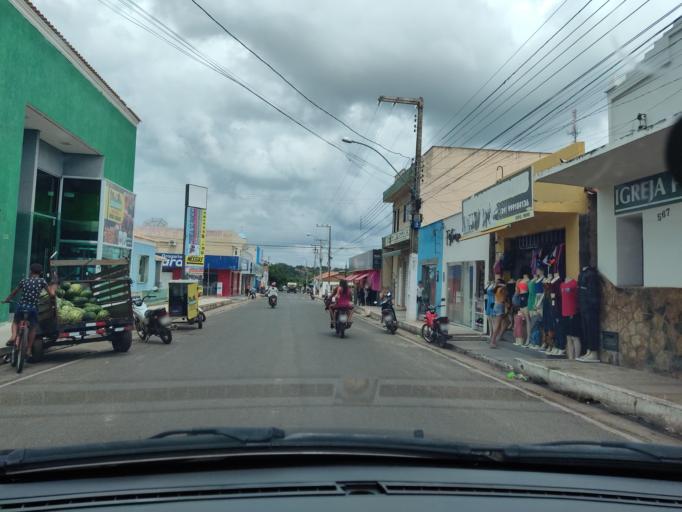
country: BR
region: Piaui
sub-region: Valenca Do Piaui
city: Valenca do Piaui
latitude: -6.4035
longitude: -41.7396
